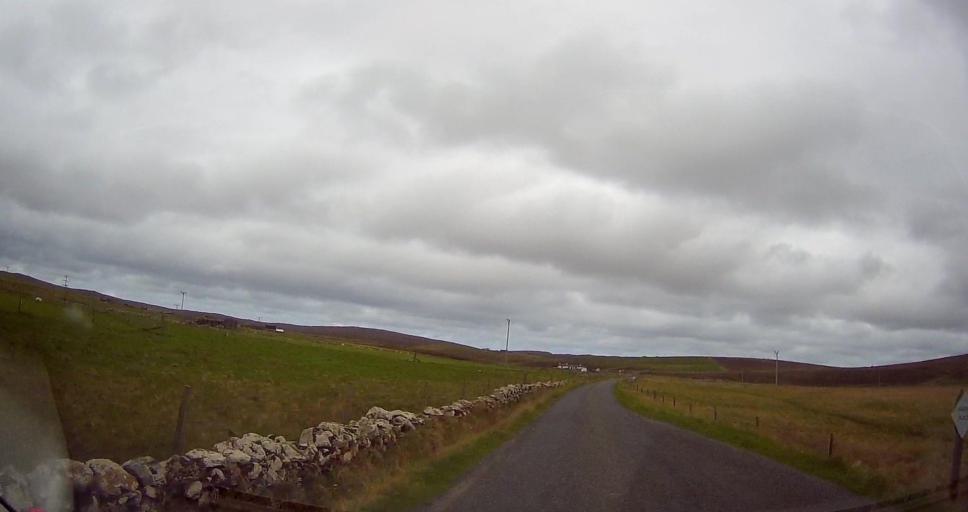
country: GB
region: Scotland
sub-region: Shetland Islands
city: Shetland
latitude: 60.7928
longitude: -0.8499
